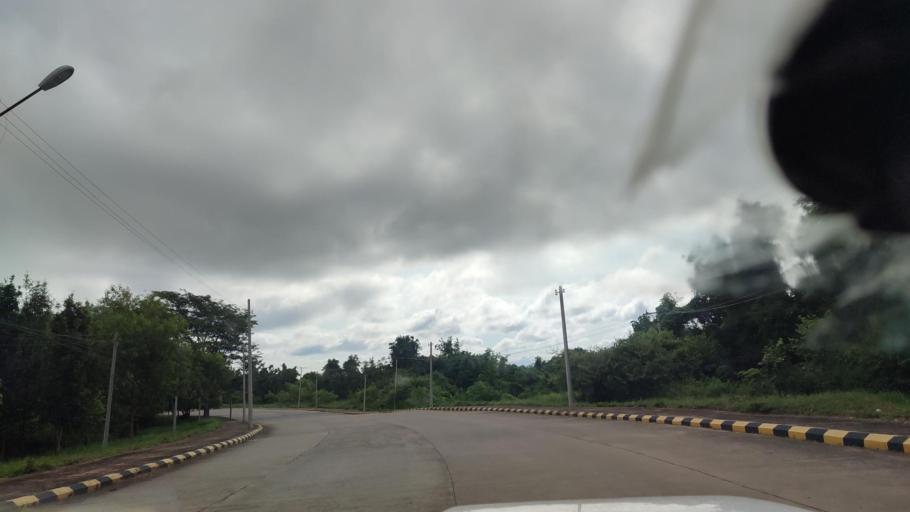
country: MM
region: Mandalay
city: Nay Pyi Taw
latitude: 19.7357
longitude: 96.0669
